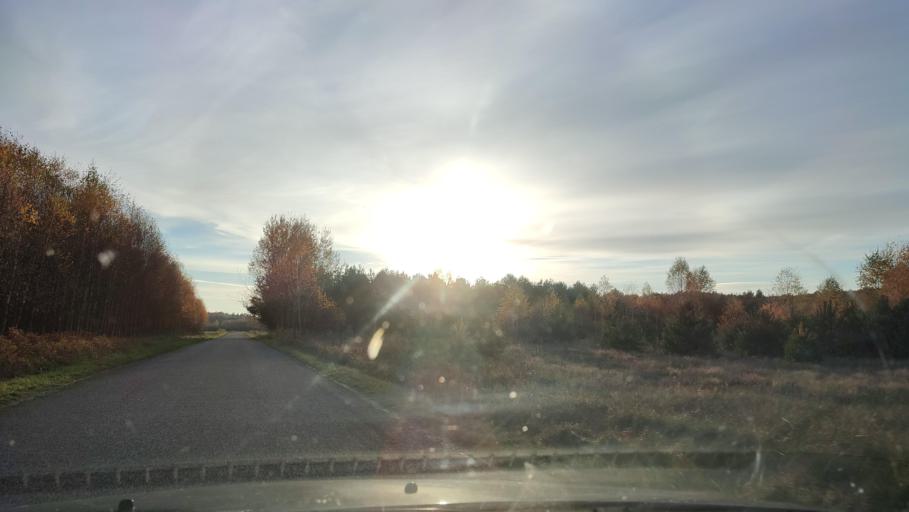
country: PL
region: Masovian Voivodeship
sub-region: Powiat przasnyski
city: Chorzele
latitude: 53.3353
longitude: 20.7455
